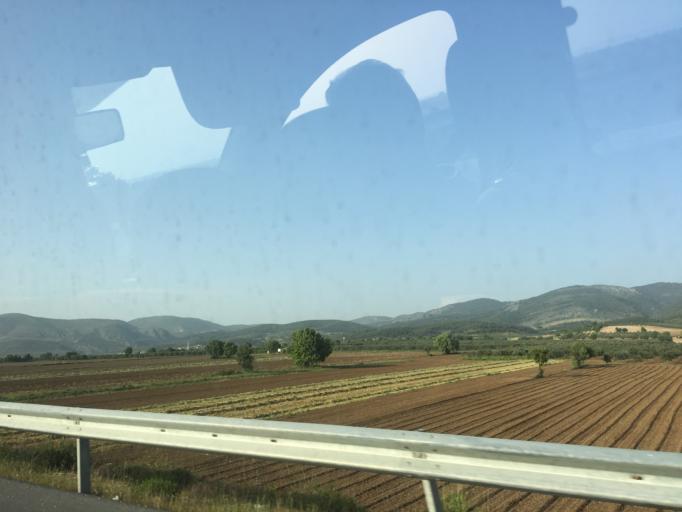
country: TR
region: Manisa
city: Golmarmara
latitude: 38.7948
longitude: 27.8980
